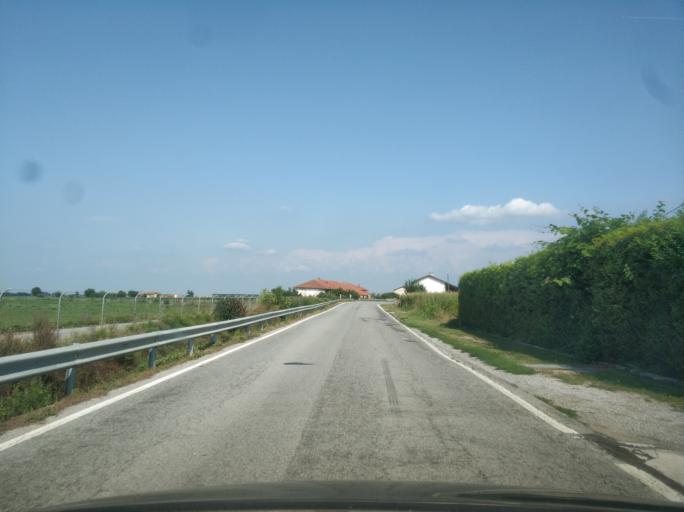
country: IT
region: Piedmont
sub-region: Provincia di Cuneo
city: Centallo
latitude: 44.5369
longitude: 7.6169
